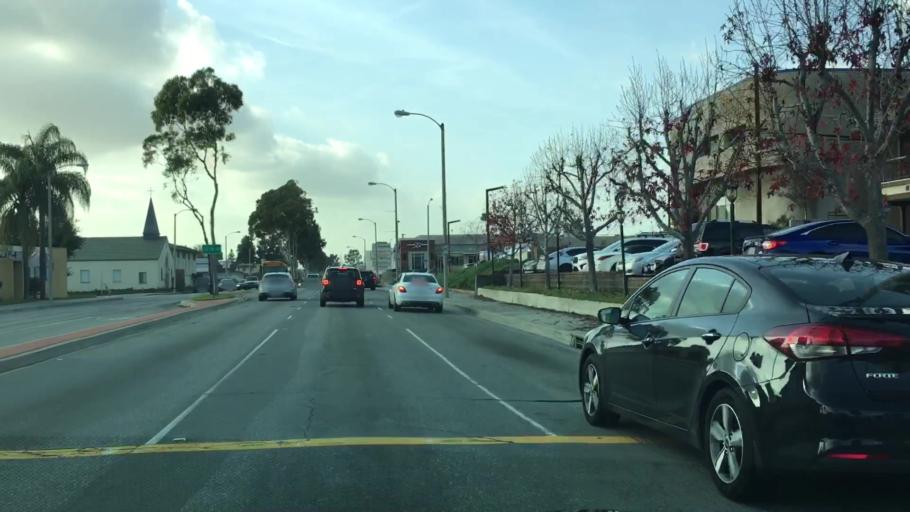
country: US
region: California
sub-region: Los Angeles County
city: Montebello
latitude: 34.0199
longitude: -118.1182
